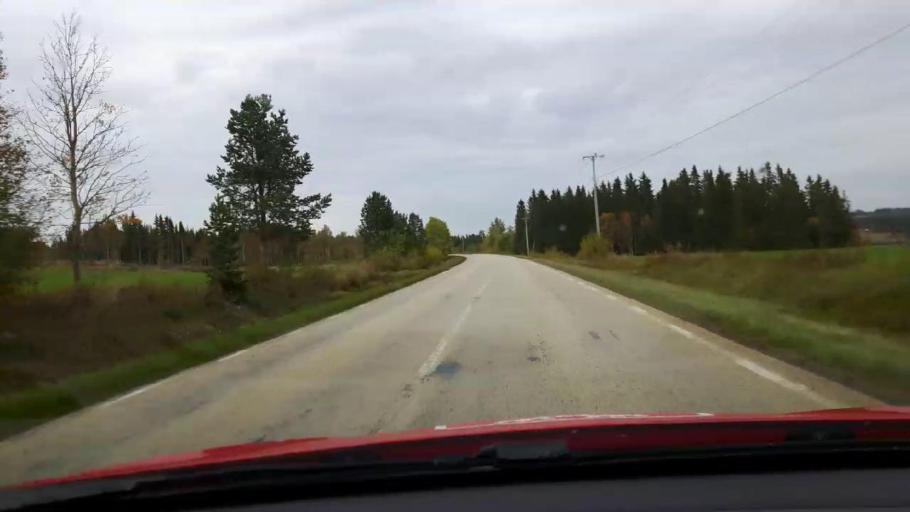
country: SE
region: Jaemtland
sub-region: Bergs Kommun
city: Hoverberg
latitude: 62.9606
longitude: 14.3464
